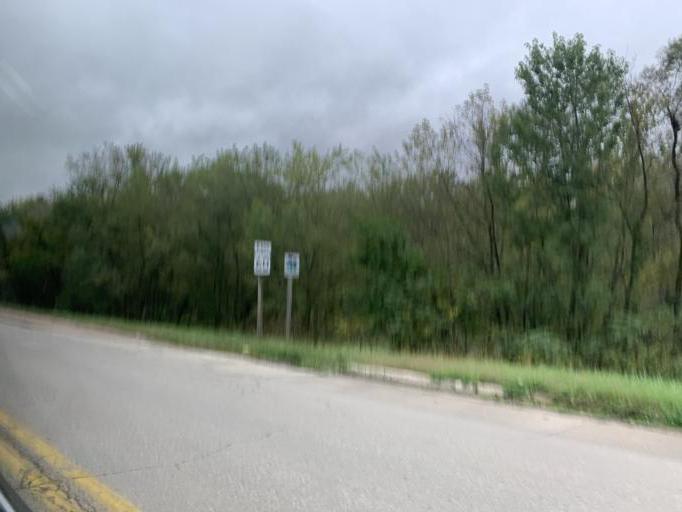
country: US
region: Wisconsin
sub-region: Grant County
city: Muscoda
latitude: 43.2030
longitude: -90.4411
